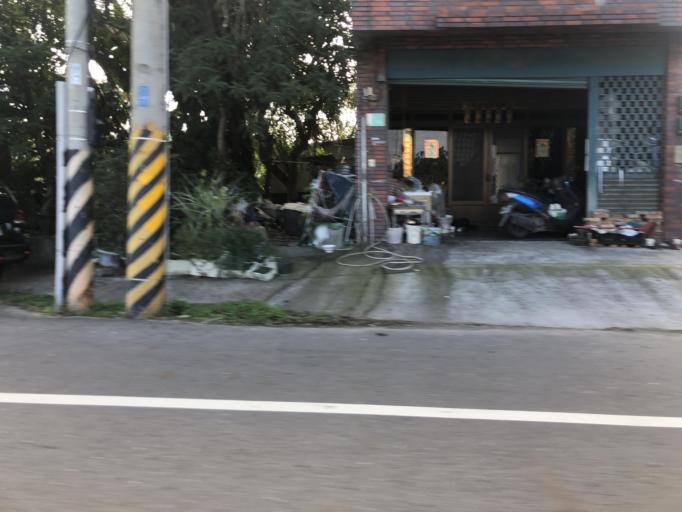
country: TW
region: Taiwan
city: Yujing
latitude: 23.0504
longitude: 120.4204
